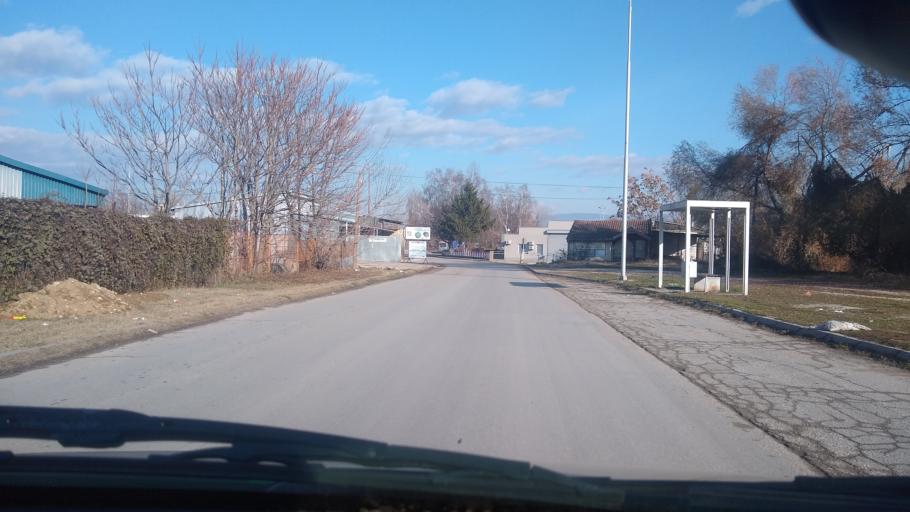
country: MK
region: Bitola
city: Bitola
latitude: 41.0124
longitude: 21.3470
